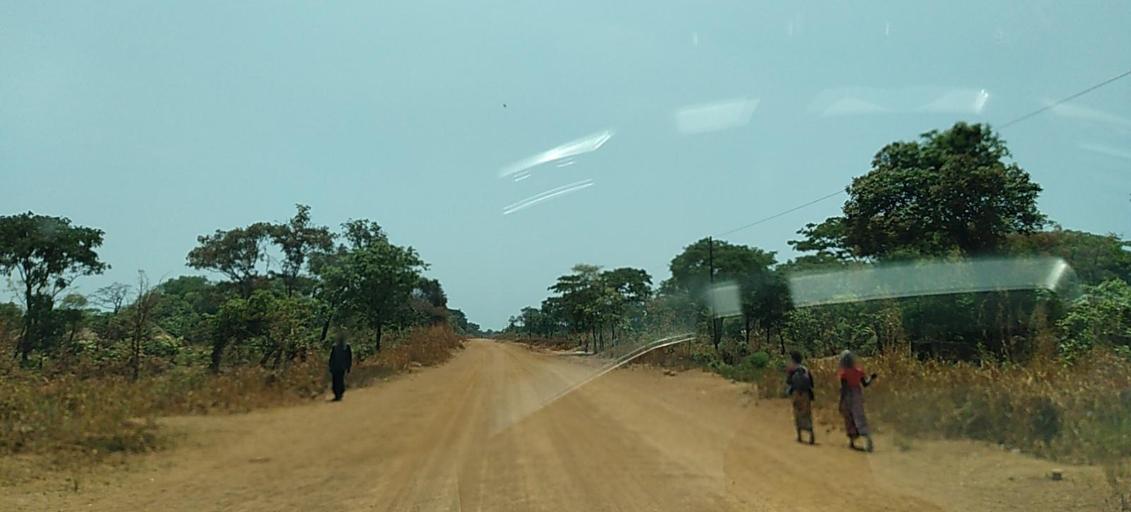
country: CD
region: Katanga
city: Kipushi
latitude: -11.9341
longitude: 26.9707
